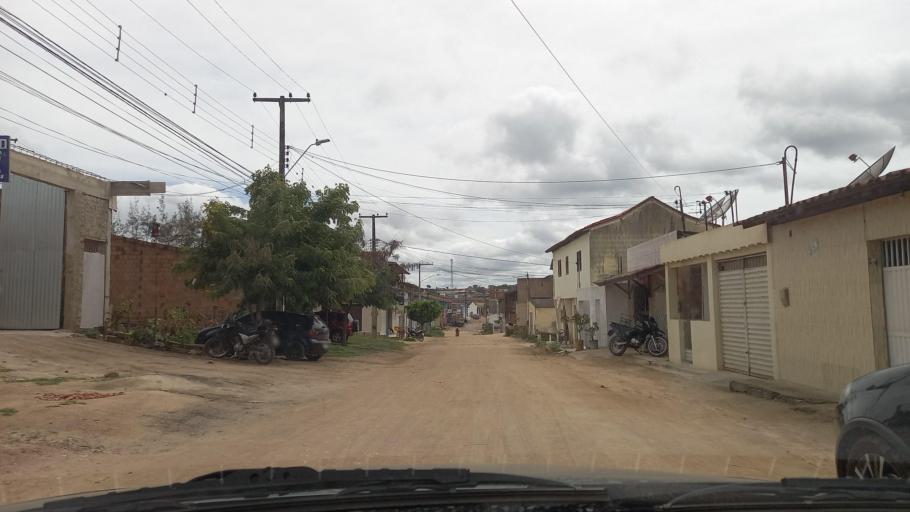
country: BR
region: Pernambuco
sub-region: Gravata
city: Gravata
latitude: -8.1959
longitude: -35.5798
